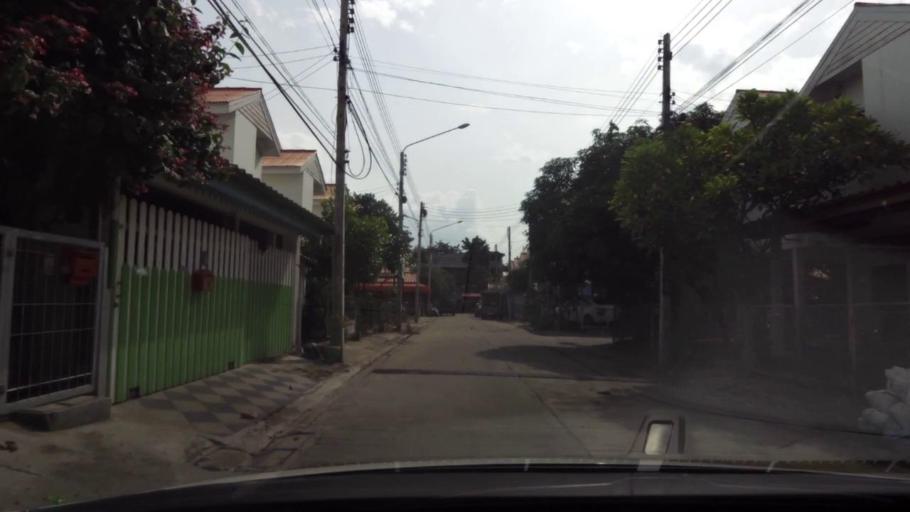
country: TH
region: Ratchaburi
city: Ratchaburi
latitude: 13.5376
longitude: 99.7917
